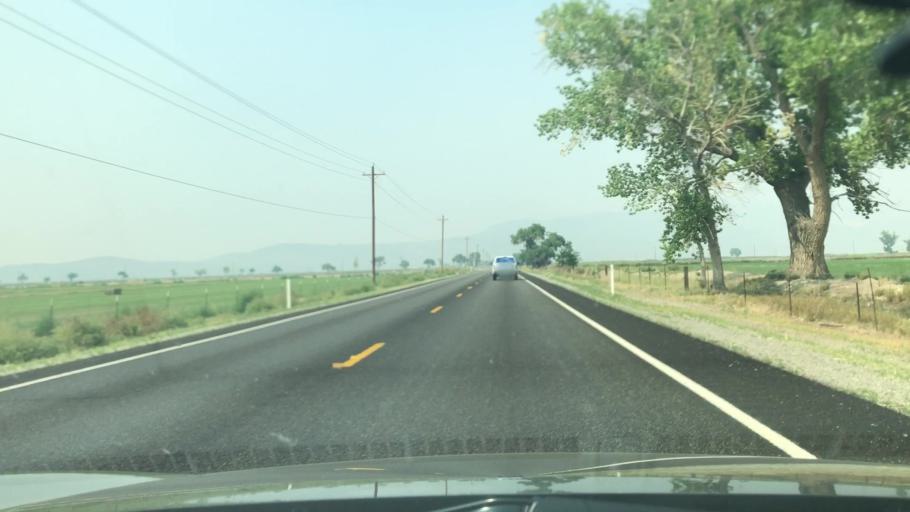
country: US
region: Nevada
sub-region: Lyon County
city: Yerington
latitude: 39.1221
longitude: -119.1810
